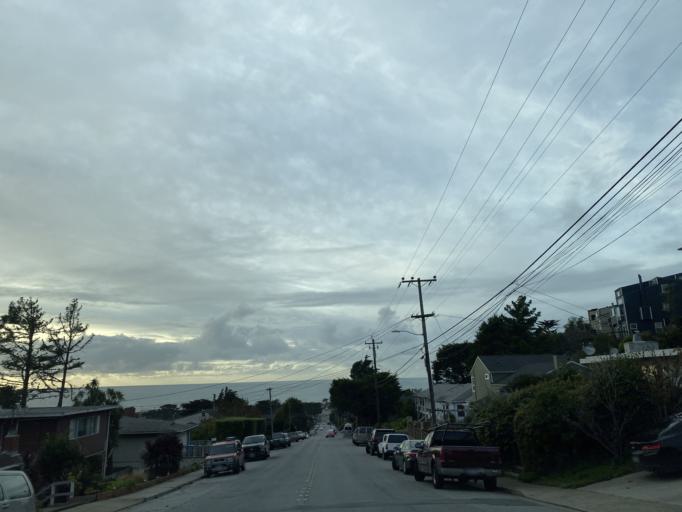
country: US
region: California
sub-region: San Mateo County
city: Colma
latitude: 37.6509
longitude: -122.4820
